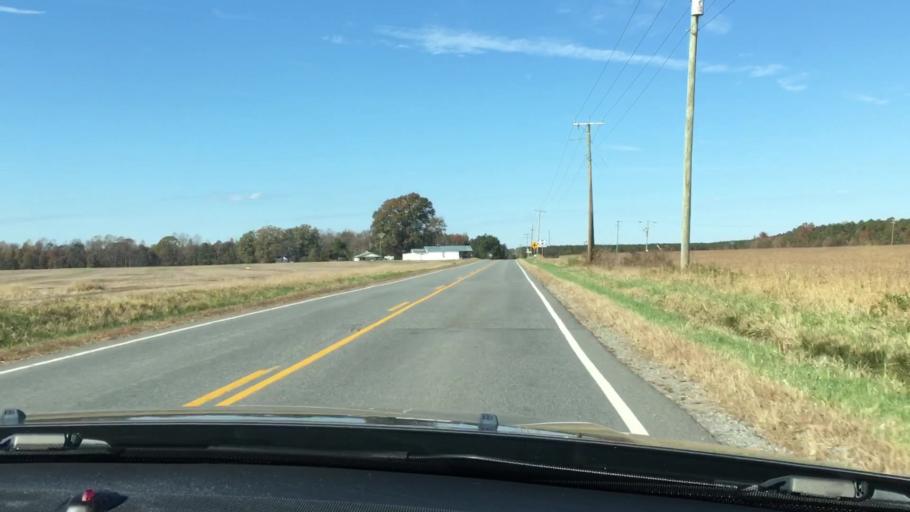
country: US
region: Virginia
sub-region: King and Queen County
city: King and Queen Court House
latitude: 37.6303
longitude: -76.9330
